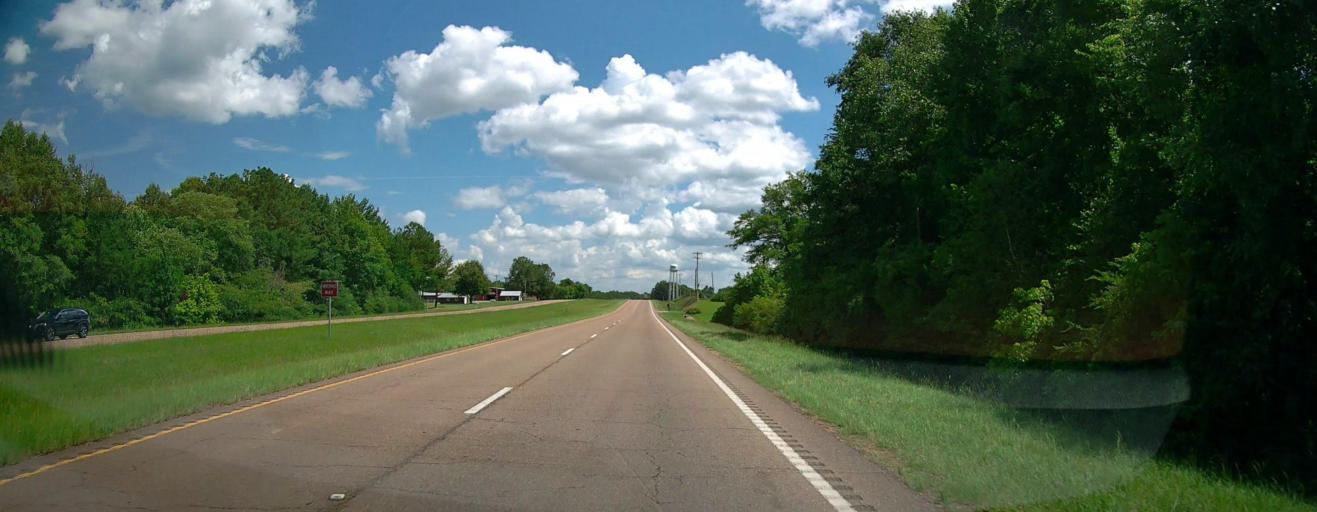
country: US
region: Mississippi
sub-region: Monroe County
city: Aberdeen
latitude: 33.7984
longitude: -88.4637
